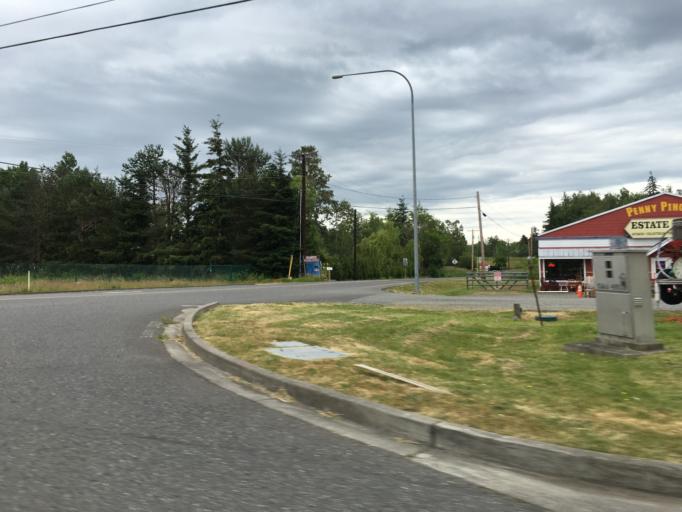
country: US
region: Washington
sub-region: Whatcom County
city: Bellingham
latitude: 48.8186
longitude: -122.4859
